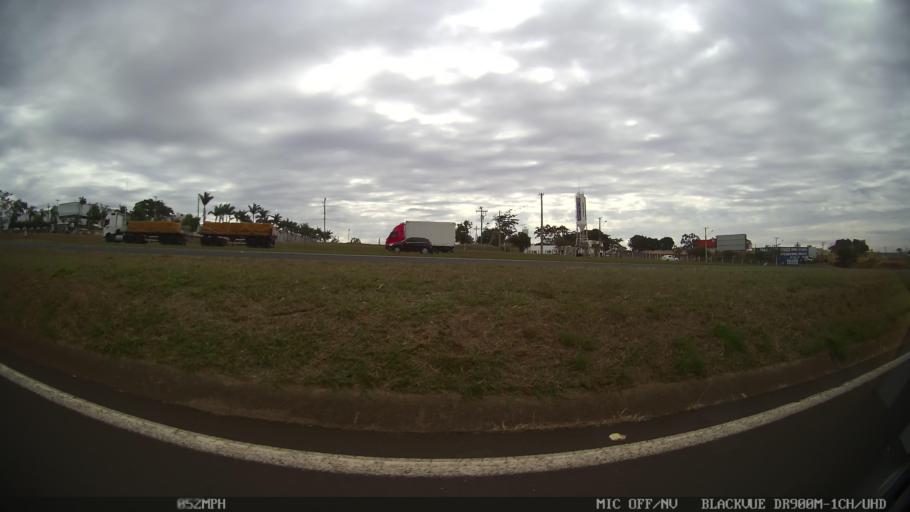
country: BR
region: Sao Paulo
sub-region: Sao Jose Do Rio Preto
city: Sao Jose do Rio Preto
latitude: -20.8126
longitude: -49.4833
